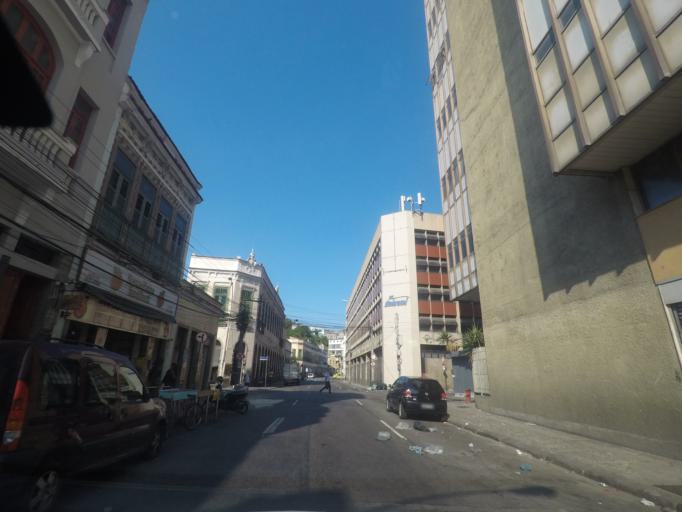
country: BR
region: Rio de Janeiro
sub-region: Rio De Janeiro
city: Rio de Janeiro
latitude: -22.9005
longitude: -43.1882
